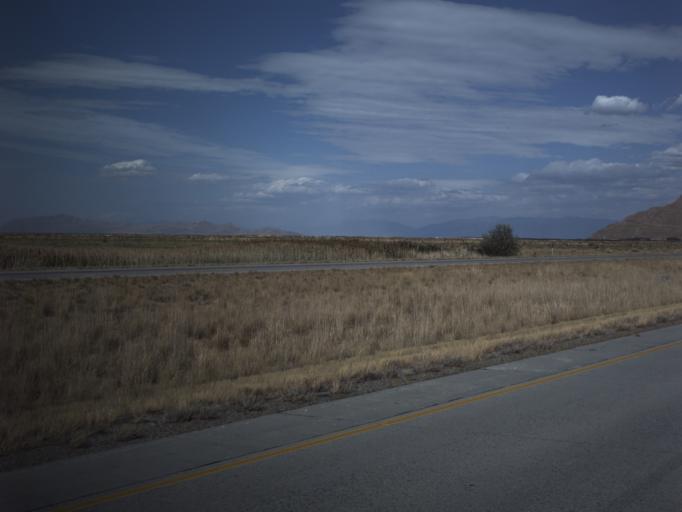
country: US
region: Utah
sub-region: Tooele County
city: Stansbury park
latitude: 40.6670
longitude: -112.3065
